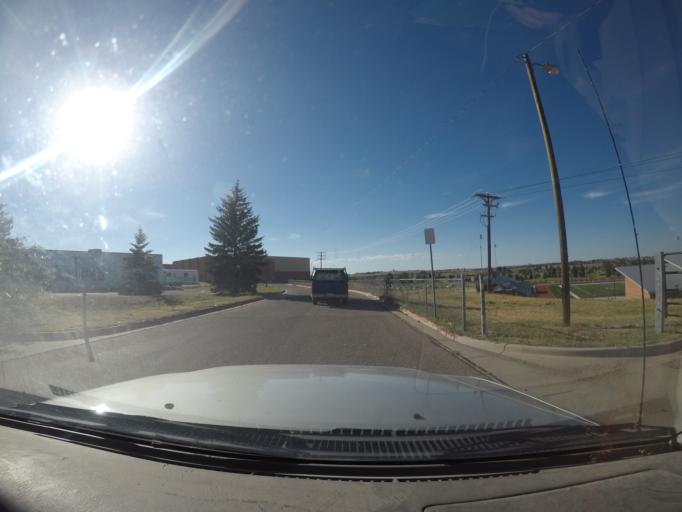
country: US
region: Wyoming
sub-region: Laramie County
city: Fox Farm-College
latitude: 41.1466
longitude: -104.7756
